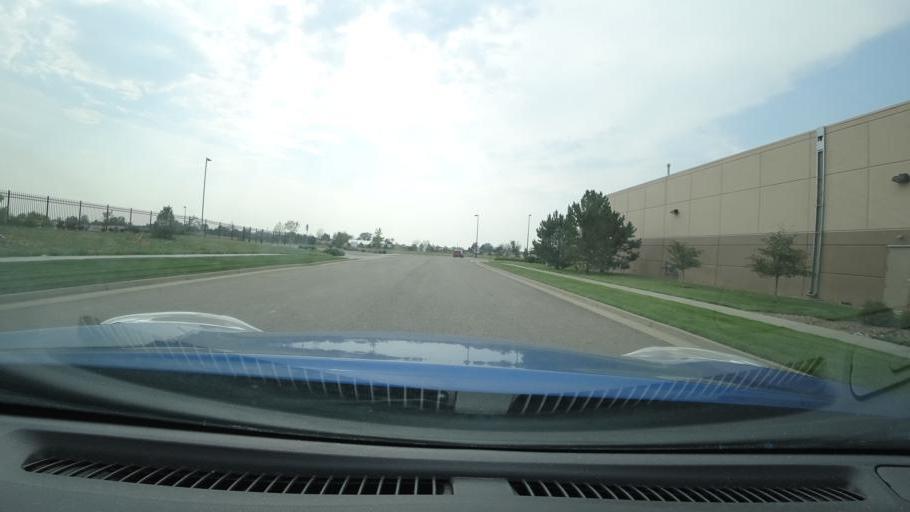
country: US
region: Colorado
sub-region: Adams County
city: Aurora
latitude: 39.7518
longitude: -104.7601
